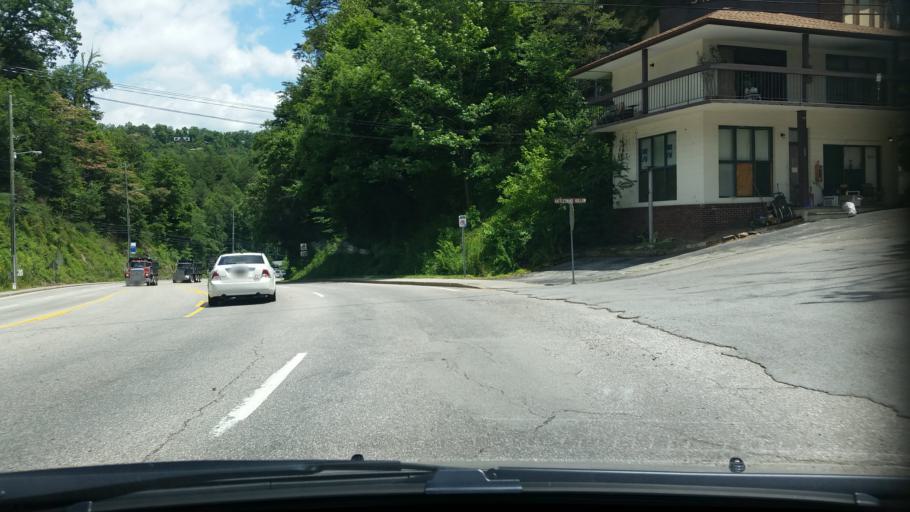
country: US
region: Tennessee
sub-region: Sevier County
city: Gatlinburg
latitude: 35.7179
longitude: -83.4997
